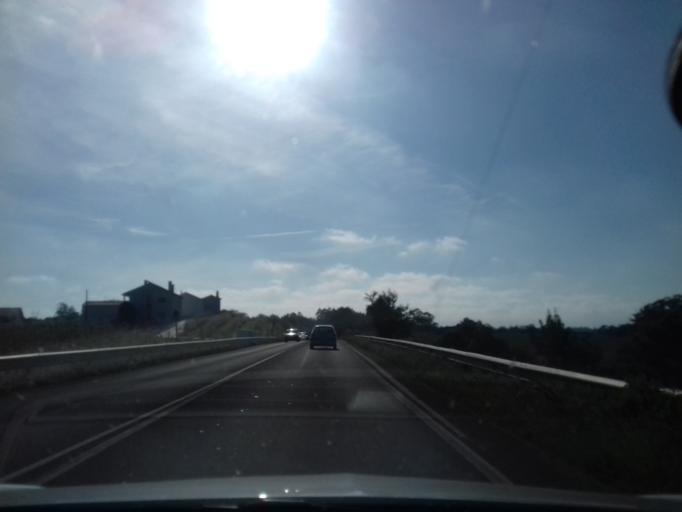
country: PT
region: Leiria
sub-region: Leiria
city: Maceira
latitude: 39.7102
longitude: -8.8547
